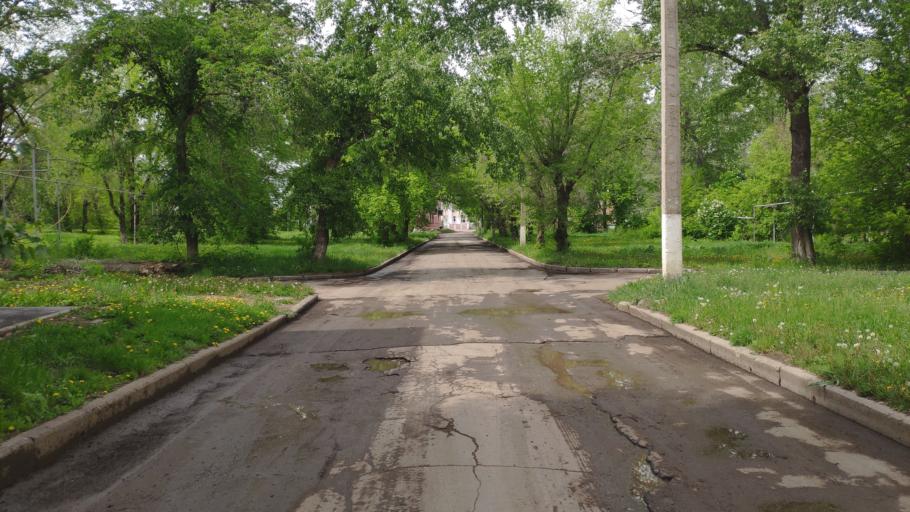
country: RU
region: Chelyabinsk
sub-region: Gorod Magnitogorsk
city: Magnitogorsk
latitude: 53.4197
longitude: 58.9548
